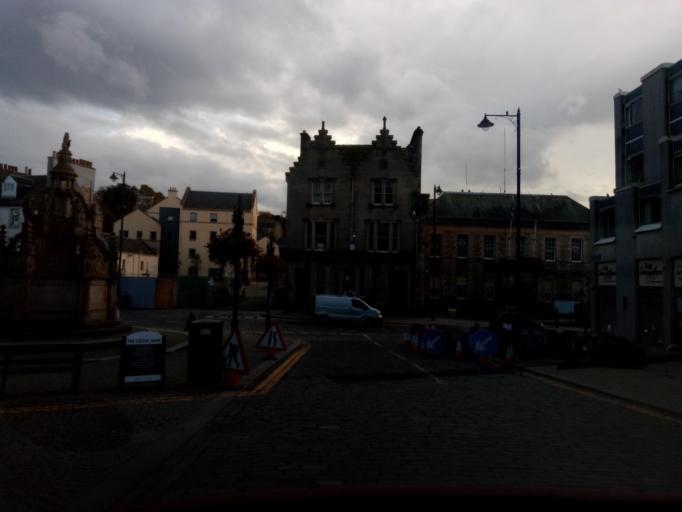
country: GB
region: Scotland
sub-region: West Lothian
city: Linlithgow
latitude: 55.9773
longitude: -3.6007
